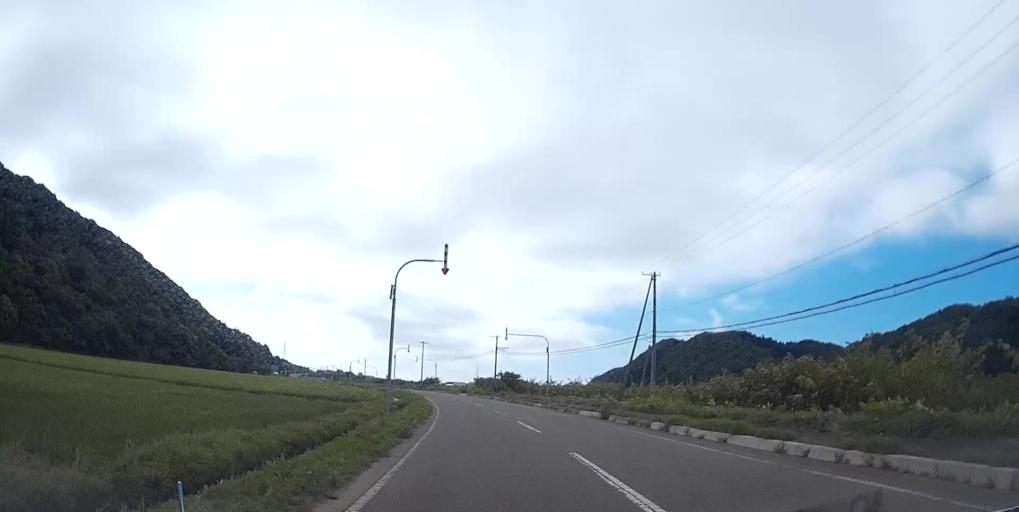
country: JP
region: Hokkaido
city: Kamiiso
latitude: 41.9722
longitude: 140.1540
